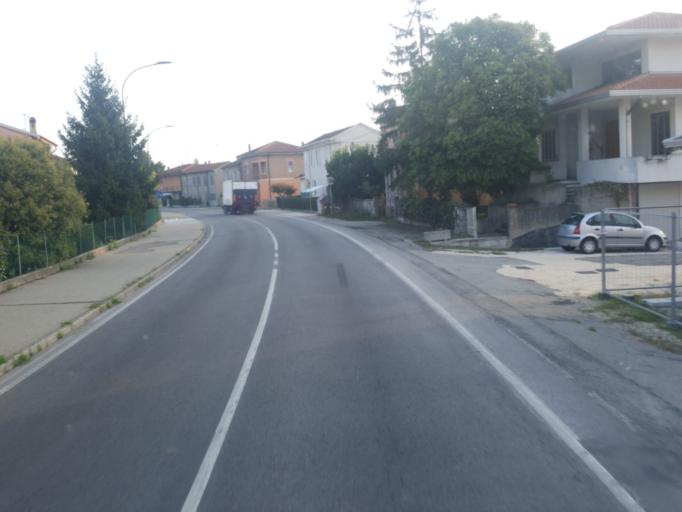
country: IT
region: Emilia-Romagna
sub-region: Provincia di Ravenna
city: Lavezzola
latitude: 44.5668
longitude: 11.8753
